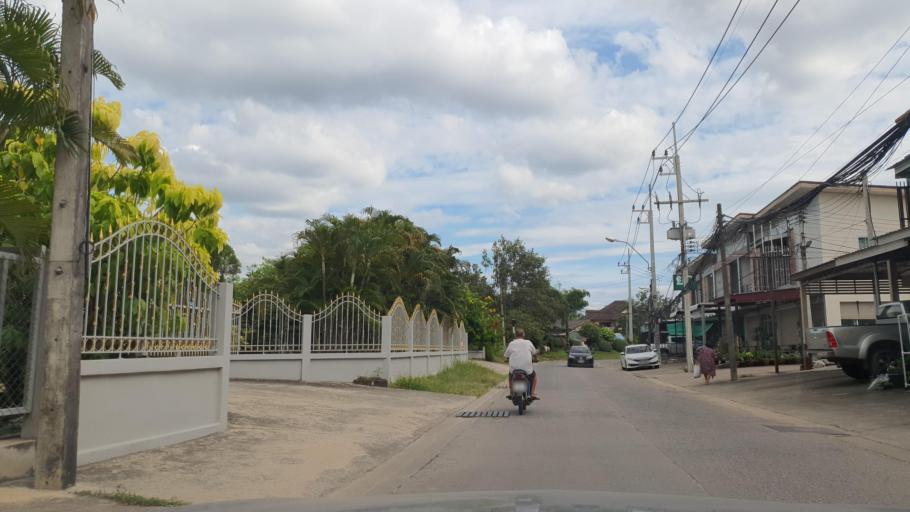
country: TH
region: Chon Buri
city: Phatthaya
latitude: 12.9554
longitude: 100.9128
